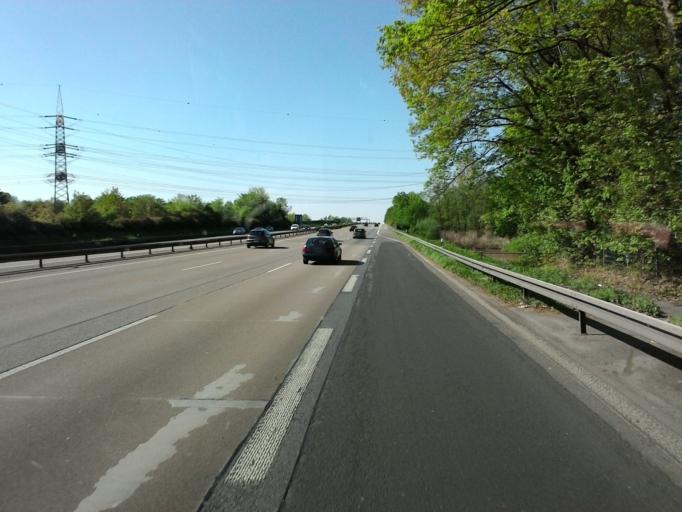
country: DE
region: North Rhine-Westphalia
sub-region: Regierungsbezirk Dusseldorf
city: Hilden
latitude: 51.1606
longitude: 6.9607
